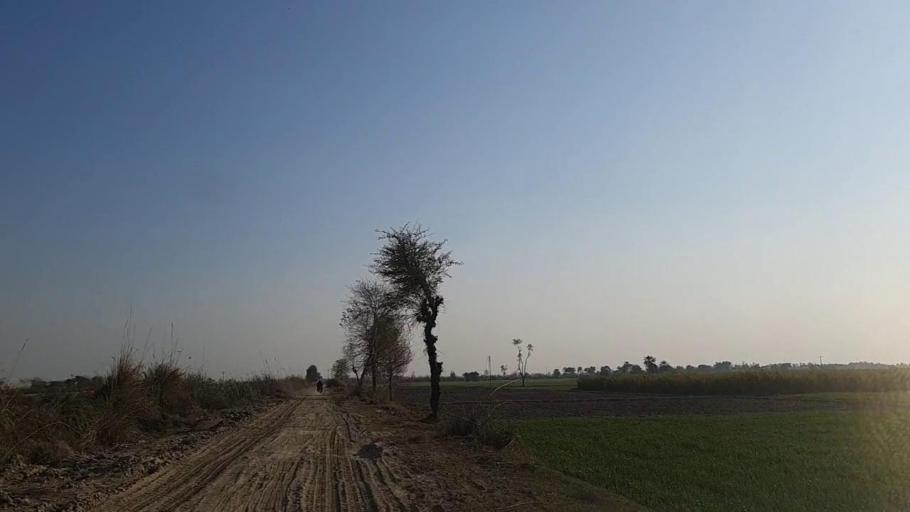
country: PK
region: Sindh
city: Daur
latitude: 26.4397
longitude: 68.3516
